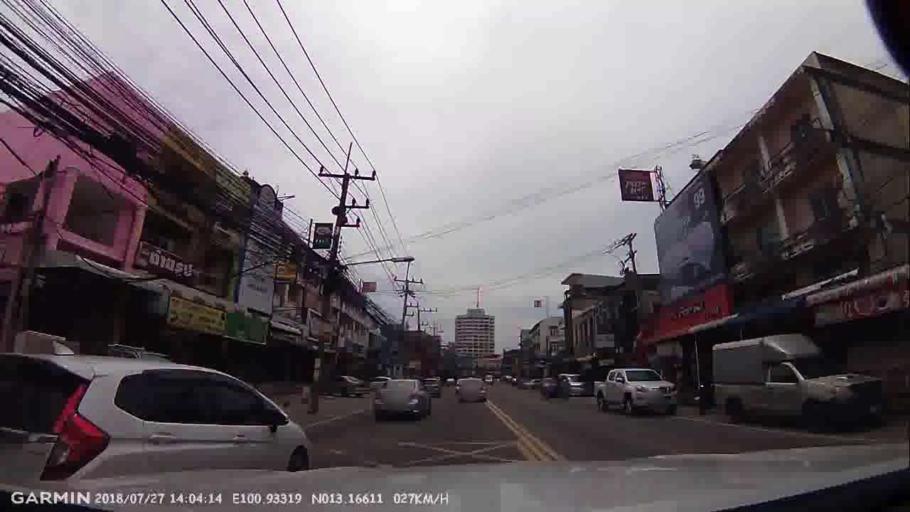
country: TH
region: Chon Buri
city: Si Racha
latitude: 13.1661
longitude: 100.9333
